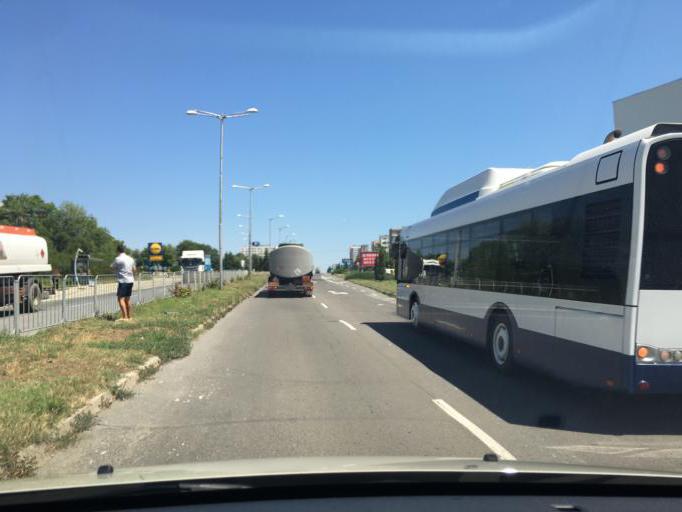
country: BG
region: Burgas
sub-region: Obshtina Burgas
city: Burgas
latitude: 42.5221
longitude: 27.4430
